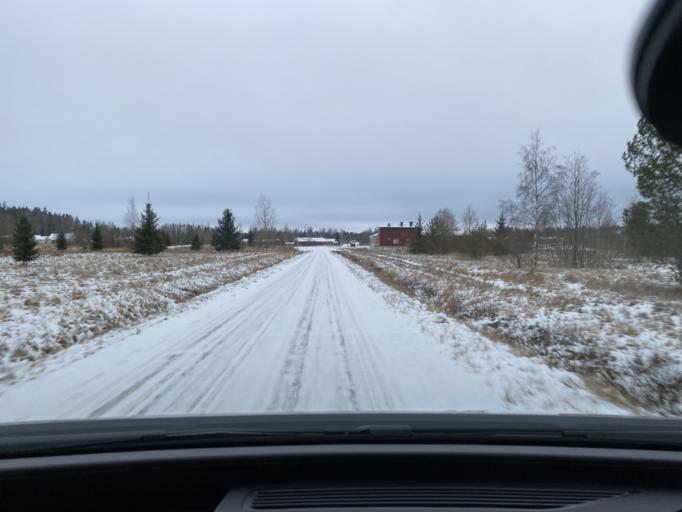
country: FI
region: Pirkanmaa
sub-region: Lounais-Pirkanmaa
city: Punkalaidun
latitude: 61.1209
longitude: 23.1159
